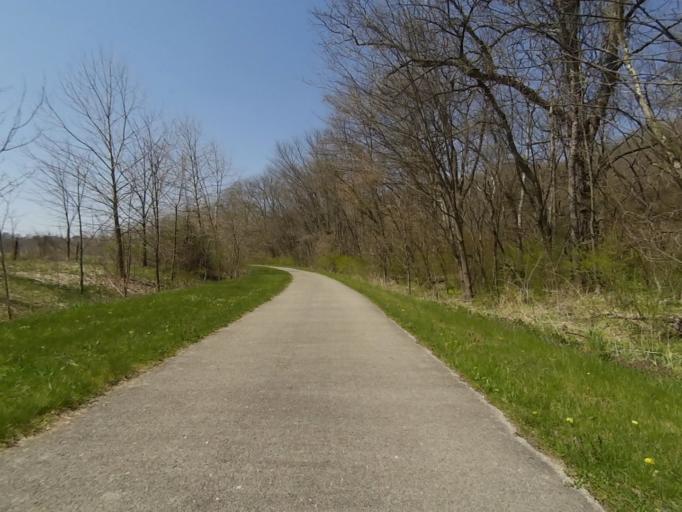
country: US
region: Pennsylvania
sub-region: Blair County
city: Williamsburg
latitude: 40.4754
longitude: -78.1929
